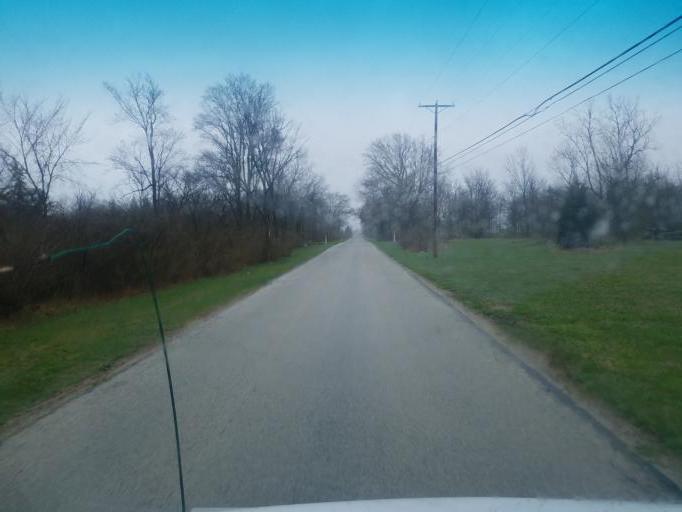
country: US
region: Ohio
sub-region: Wood County
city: North Baltimore
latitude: 41.2446
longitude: -83.6308
